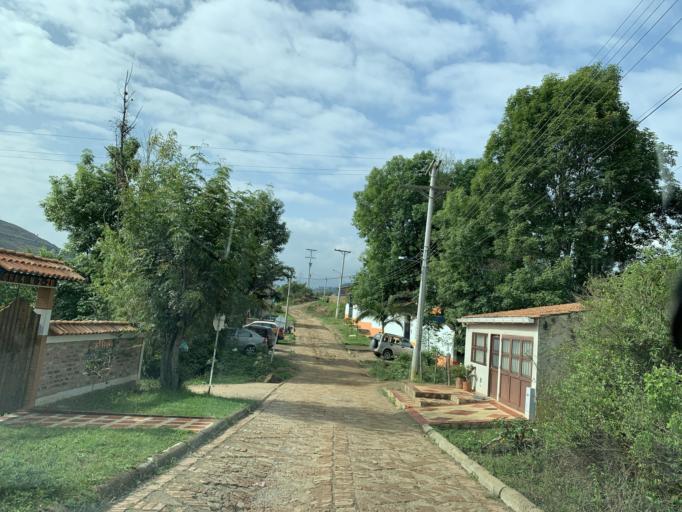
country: CO
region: Boyaca
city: Raquira
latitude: 5.5780
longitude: -73.6471
